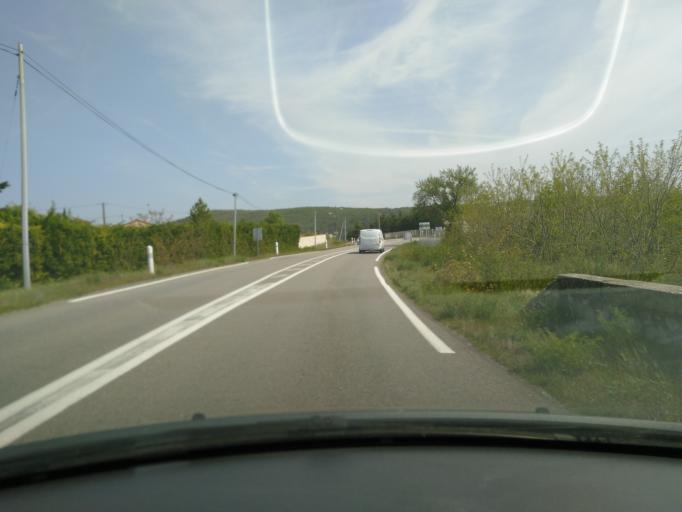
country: FR
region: Rhone-Alpes
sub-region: Departement de l'Ardeche
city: Alba-la-Romaine
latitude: 44.5674
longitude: 4.5993
